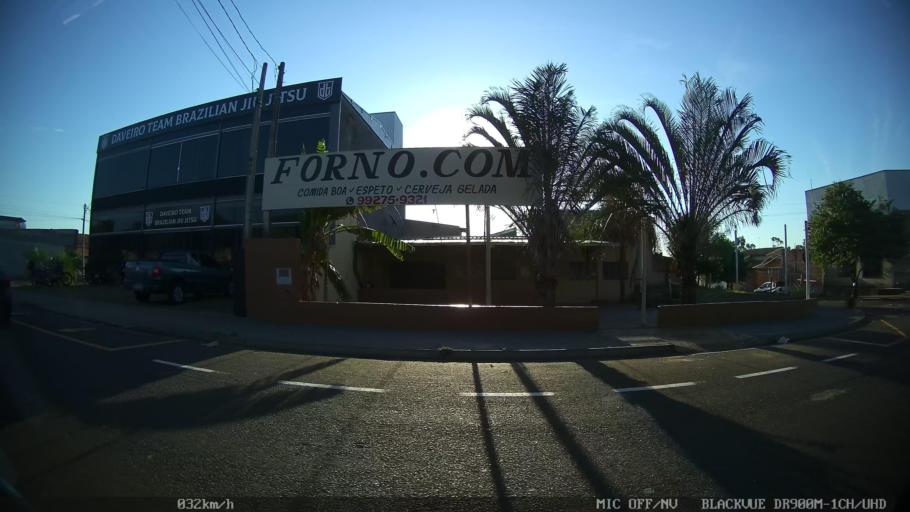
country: BR
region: Sao Paulo
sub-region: Sao Jose Do Rio Preto
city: Sao Jose do Rio Preto
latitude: -20.7880
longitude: -49.3467
